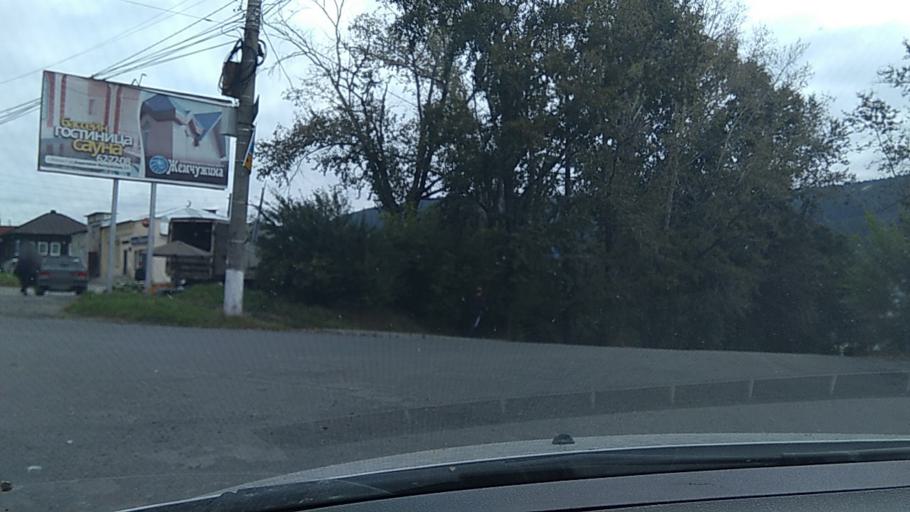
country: RU
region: Chelyabinsk
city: Zlatoust
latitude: 55.1781
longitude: 59.7009
